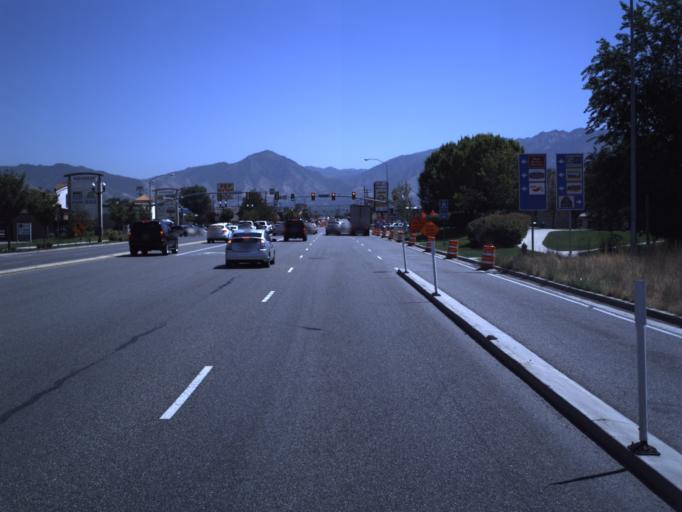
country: US
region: Utah
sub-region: Salt Lake County
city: Taylorsville
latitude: 40.6966
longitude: -111.9491
